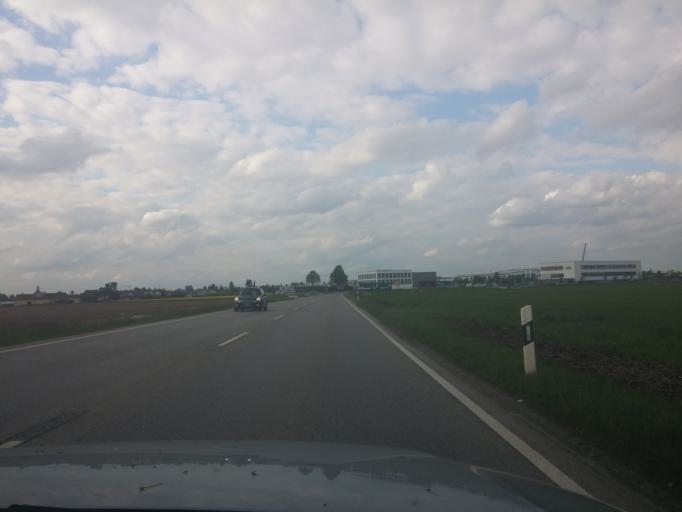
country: DE
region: Bavaria
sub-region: Upper Bavaria
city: Feldkirchen
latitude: 48.1368
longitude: 11.7360
